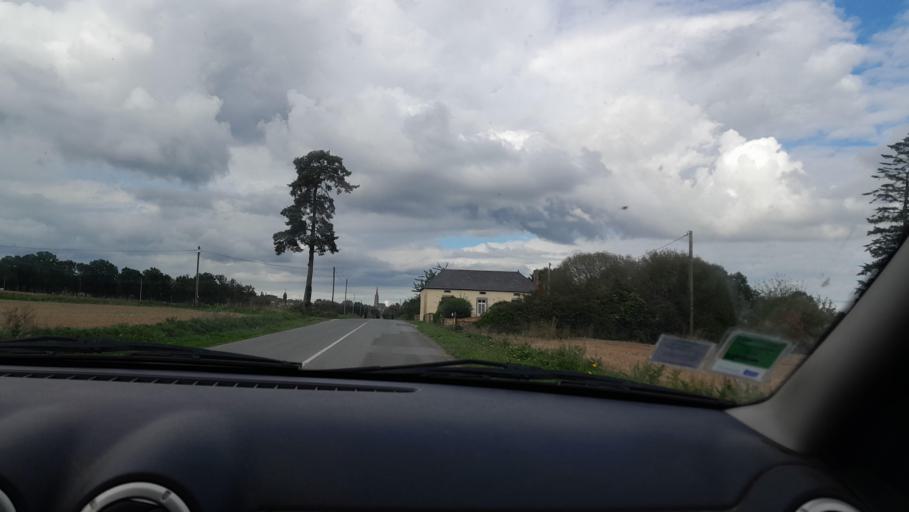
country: FR
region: Brittany
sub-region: Departement d'Ille-et-Vilaine
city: Le Pertre
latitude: 48.0159
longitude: -1.0379
